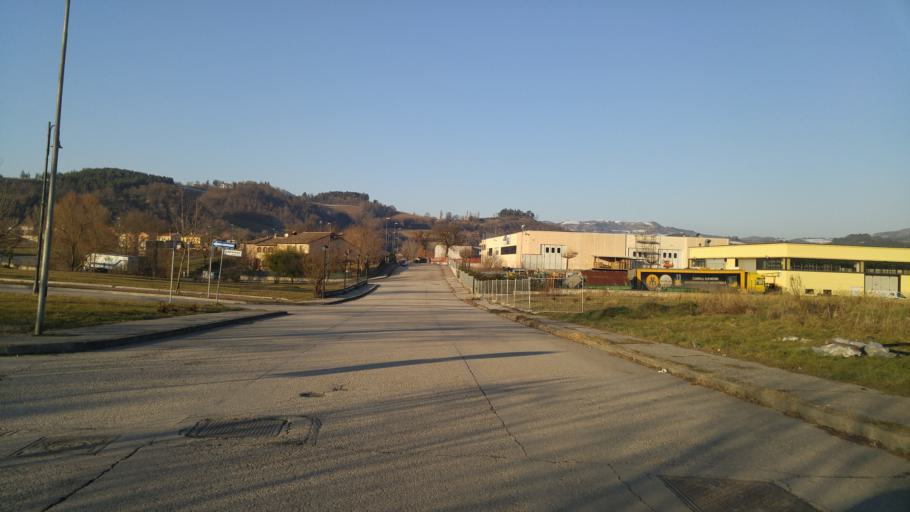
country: IT
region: The Marches
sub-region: Provincia di Pesaro e Urbino
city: Fermignano
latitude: 43.6869
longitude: 12.6464
